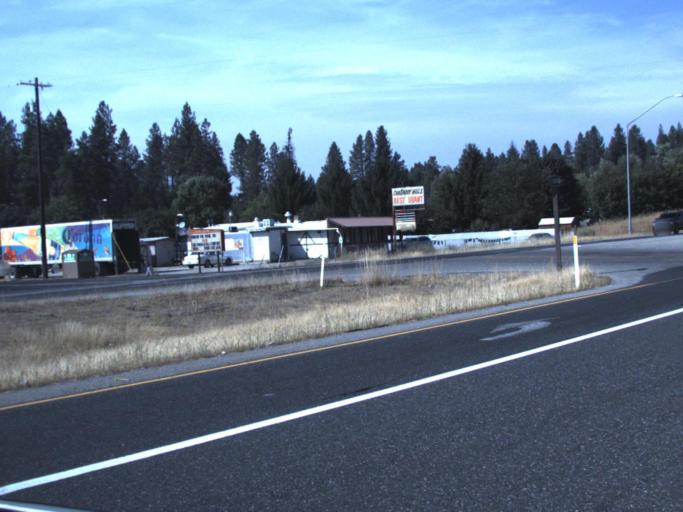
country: US
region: Washington
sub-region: Spokane County
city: Deer Park
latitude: 47.9036
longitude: -117.3511
